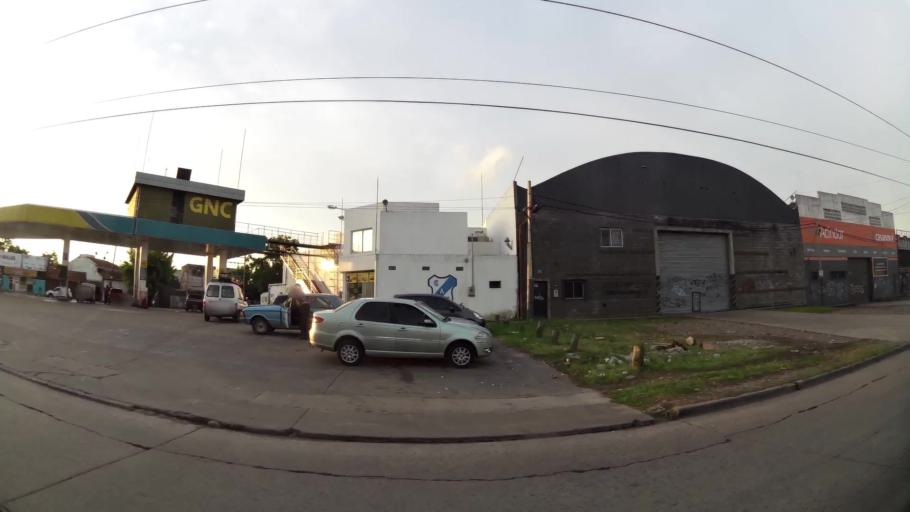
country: AR
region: Buenos Aires
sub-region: Partido de Lomas de Zamora
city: Lomas de Zamora
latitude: -34.7647
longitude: -58.3679
